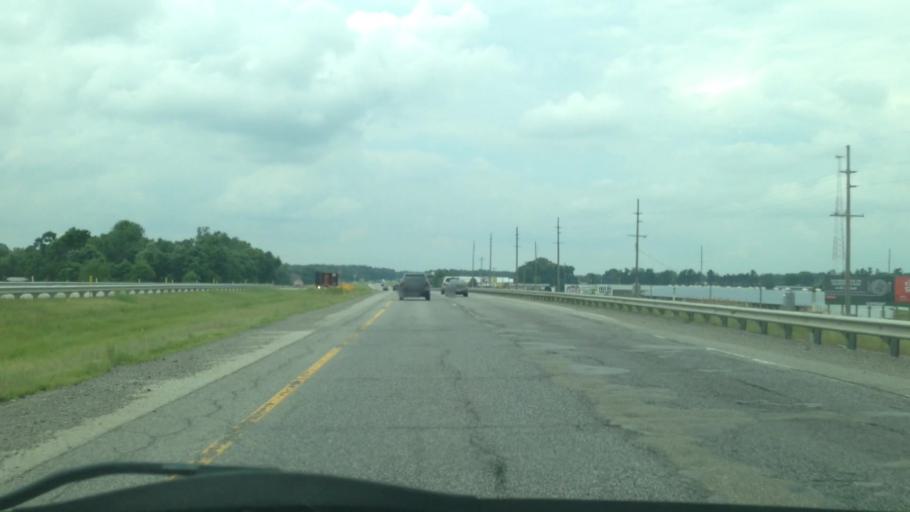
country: US
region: Indiana
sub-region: Elkhart County
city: Middlebury
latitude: 41.7432
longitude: -85.7270
